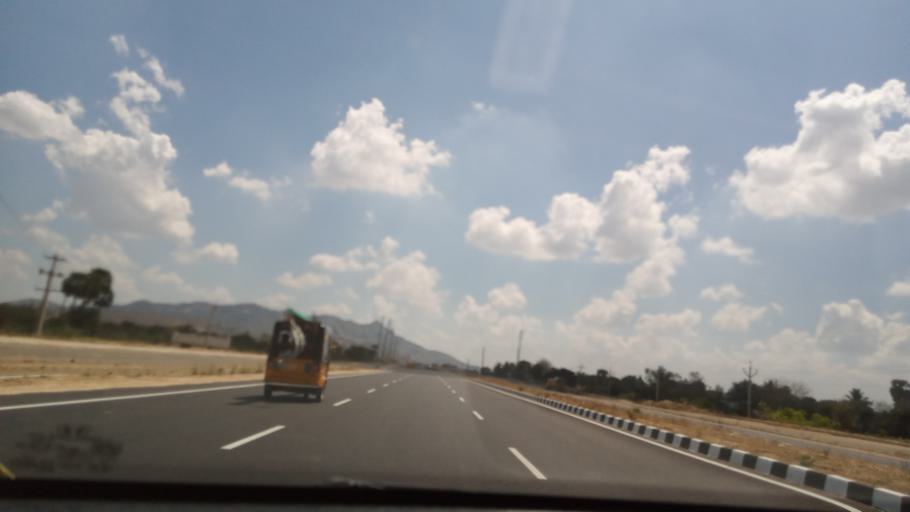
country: IN
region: Andhra Pradesh
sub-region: Chittoor
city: Pakala
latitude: 13.3614
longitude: 79.0879
